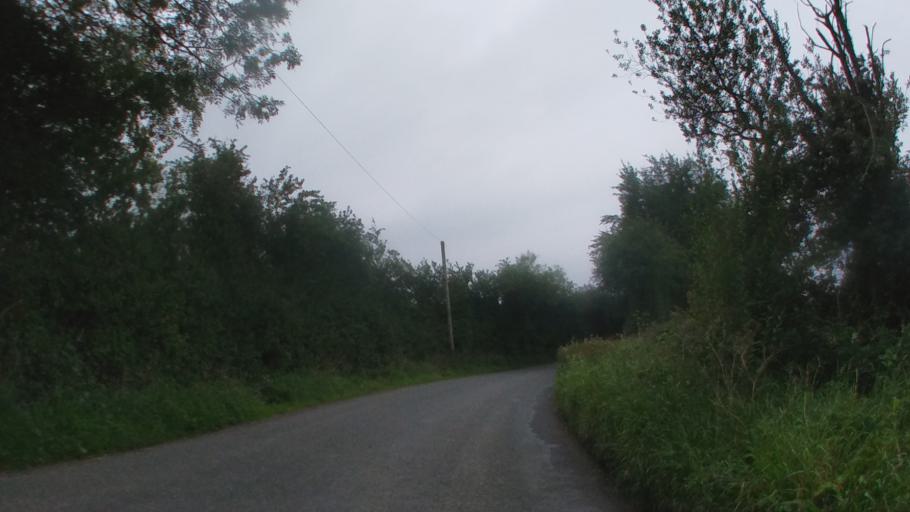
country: IE
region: Leinster
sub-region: Kilkenny
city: Kilkenny
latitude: 52.6991
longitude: -7.1937
